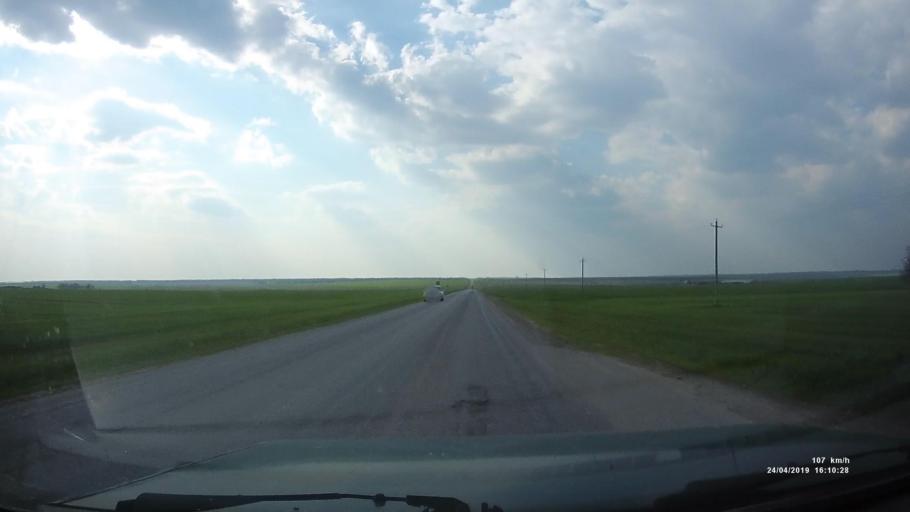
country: RU
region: Rostov
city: Sovetskoye
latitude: 46.7175
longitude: 42.2696
